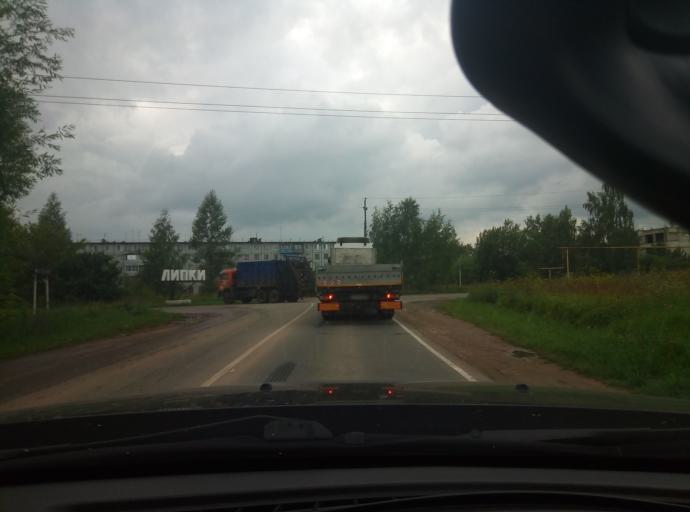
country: RU
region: Tula
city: Lomintsevskiy
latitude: 53.9524
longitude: 37.7018
